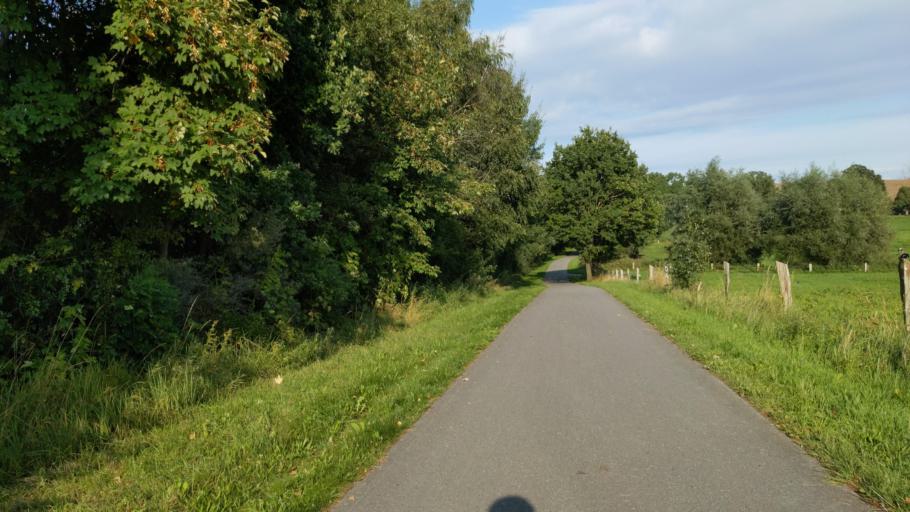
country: DE
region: Mecklenburg-Vorpommern
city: Kalkhorst
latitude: 54.0049
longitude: 11.0374
